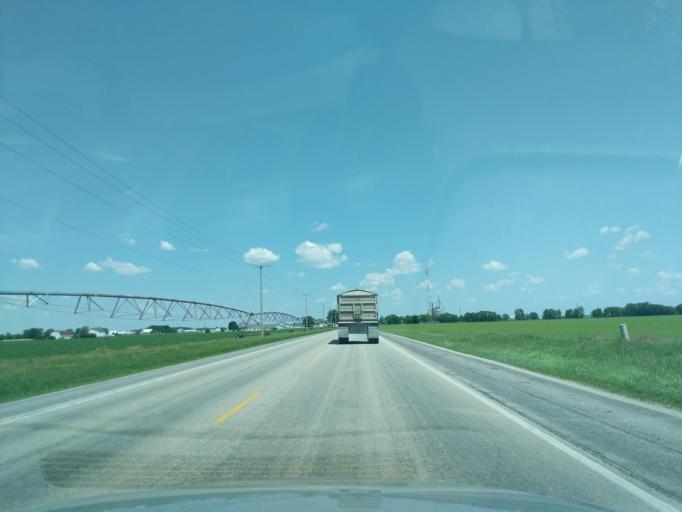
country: US
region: Indiana
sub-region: LaGrange County
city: Topeka
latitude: 41.5279
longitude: -85.5778
